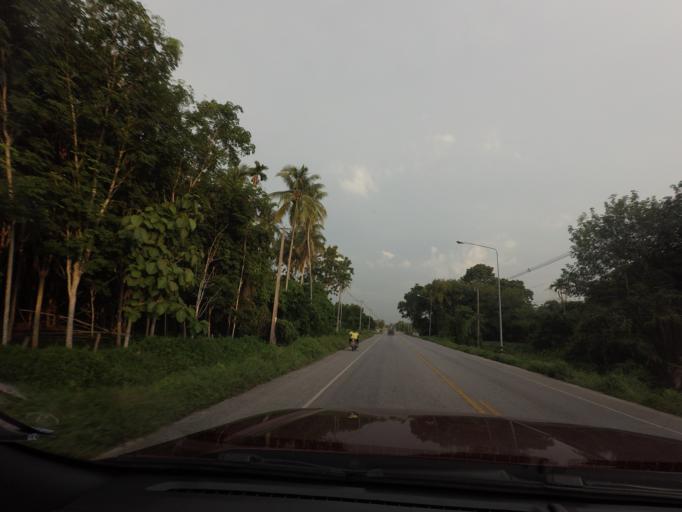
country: TH
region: Pattani
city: Mae Lan
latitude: 6.6279
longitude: 101.1875
